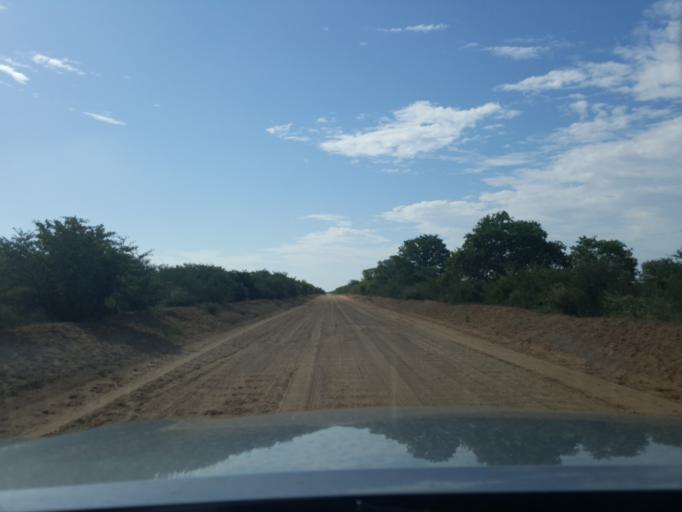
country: BW
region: Kweneng
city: Khudumelapye
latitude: -23.5057
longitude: 24.7093
